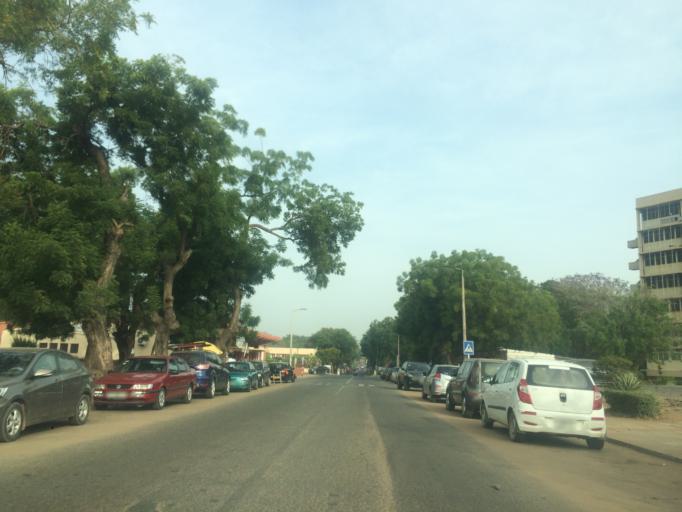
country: GH
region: Greater Accra
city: Accra
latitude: 5.5376
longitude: -0.2275
